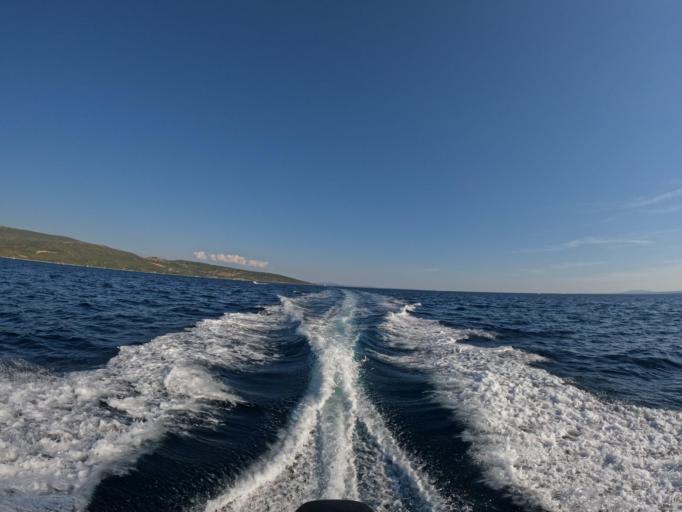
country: HR
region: Primorsko-Goranska
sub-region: Grad Krk
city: Krk
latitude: 45.0069
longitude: 14.5928
